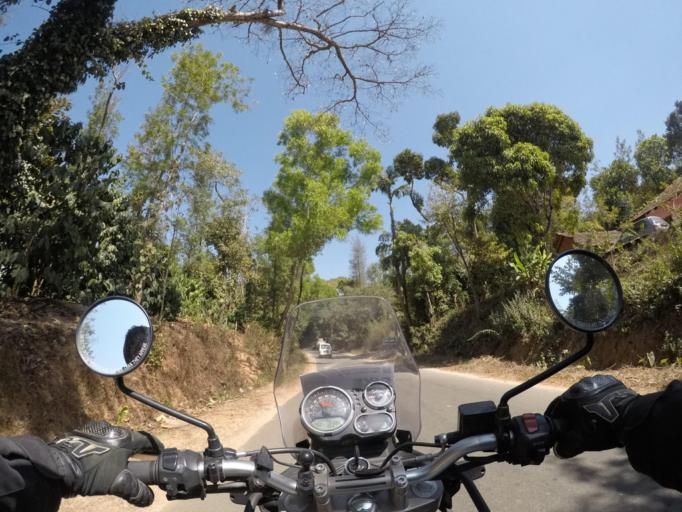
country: IN
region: Karnataka
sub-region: Chikmagalur
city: Mudigere
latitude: 13.0658
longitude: 75.6770
